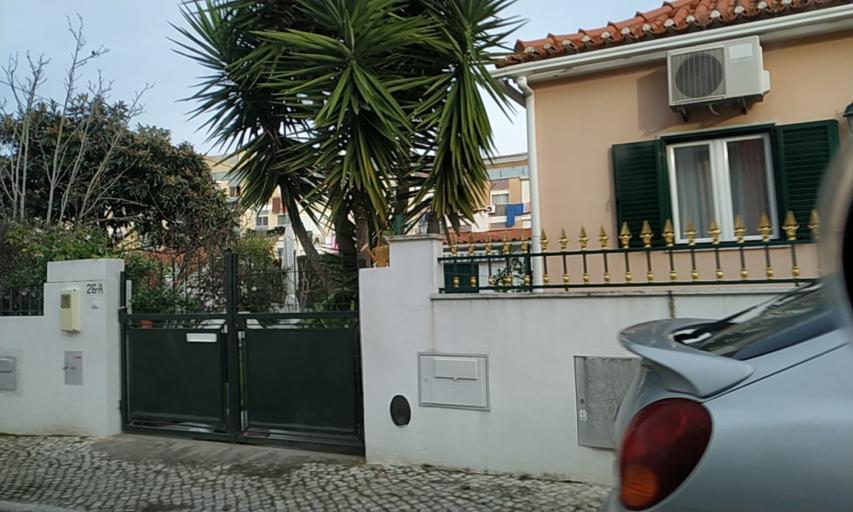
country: PT
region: Setubal
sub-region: Setubal
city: Setubal
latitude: 38.5220
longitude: -8.8759
